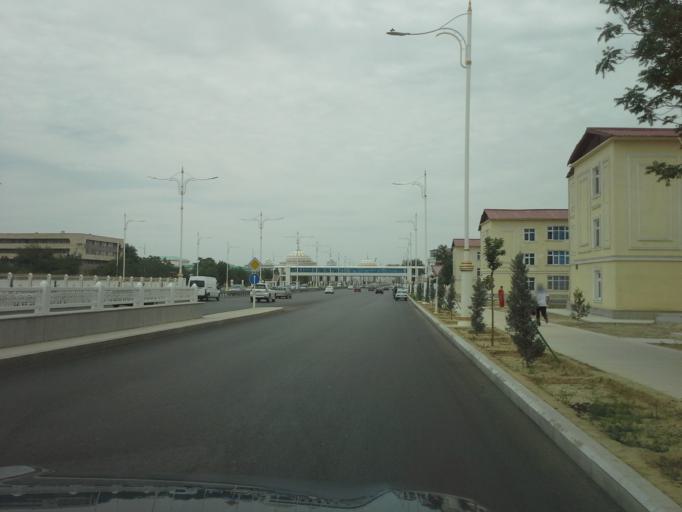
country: TM
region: Ahal
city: Ashgabat
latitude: 37.9237
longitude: 58.3904
